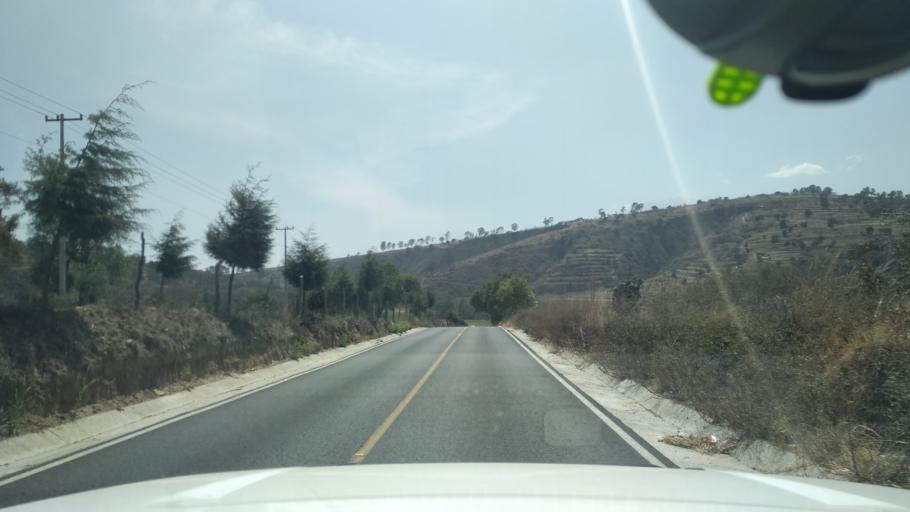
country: MX
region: Puebla
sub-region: San Matias Tlalancaleca
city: San Francisco Tlaloc
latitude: 19.3652
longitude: -98.4556
